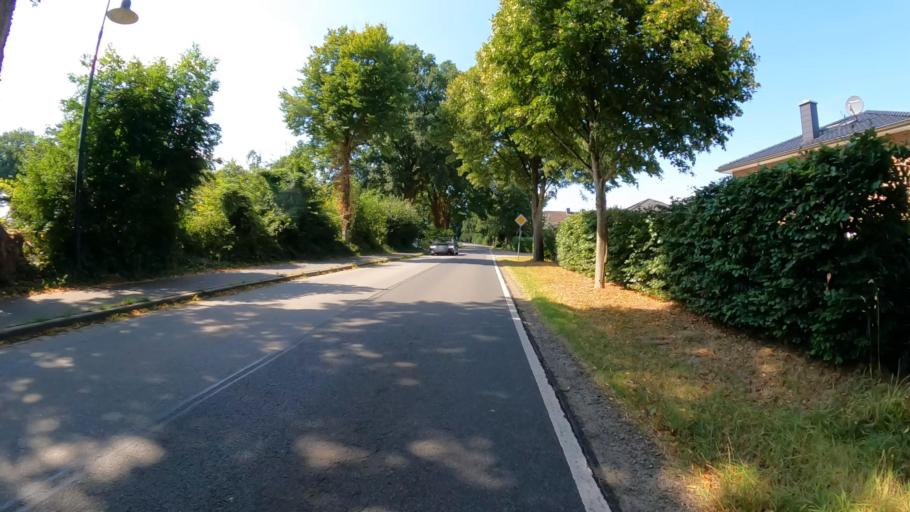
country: DE
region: Schleswig-Holstein
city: Seeth-Ekholt
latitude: 53.7428
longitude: 9.7296
